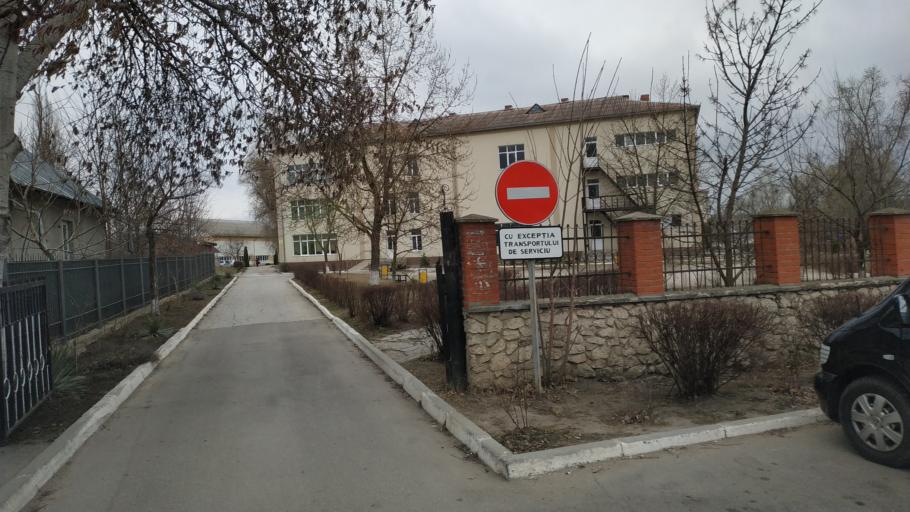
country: MD
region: Laloveni
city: Ialoveni
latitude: 46.9417
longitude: 28.7753
